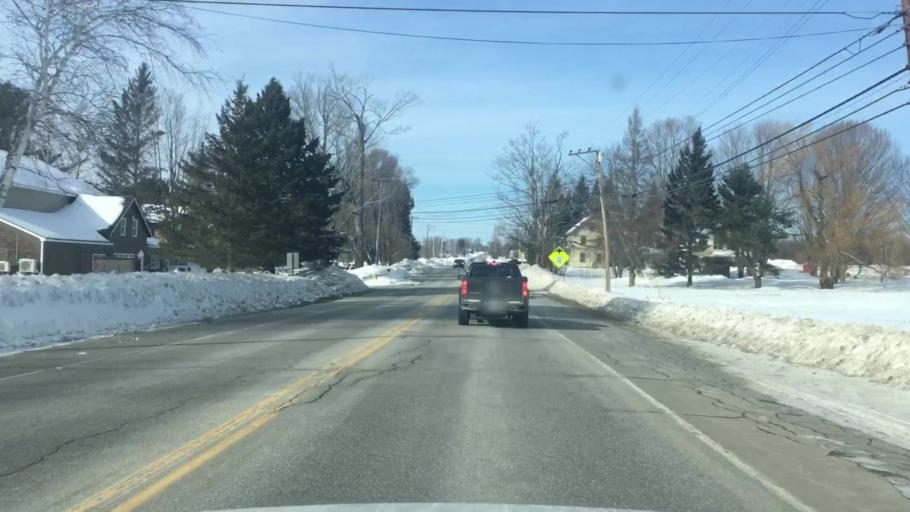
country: US
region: Maine
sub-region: Penobscot County
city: Charleston
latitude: 45.0143
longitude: -69.0272
